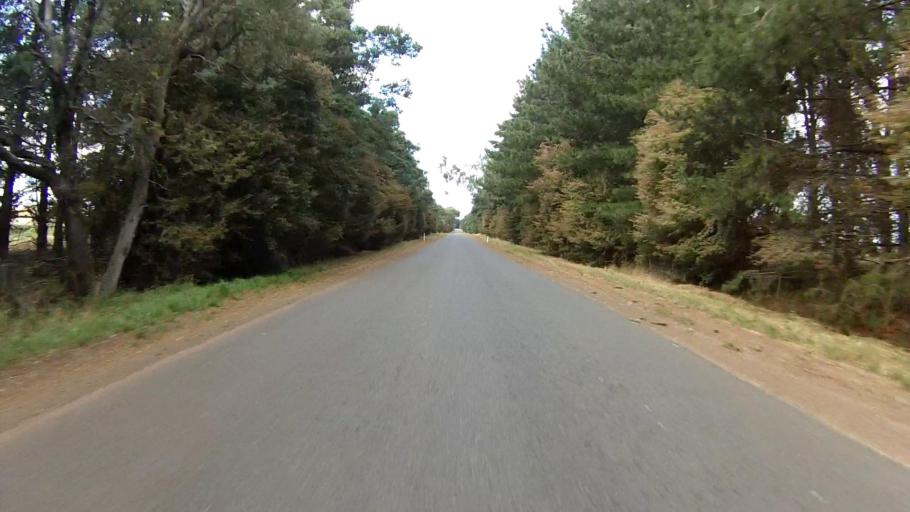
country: AU
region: Tasmania
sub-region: Northern Midlands
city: Evandale
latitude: -41.6861
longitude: 147.3593
